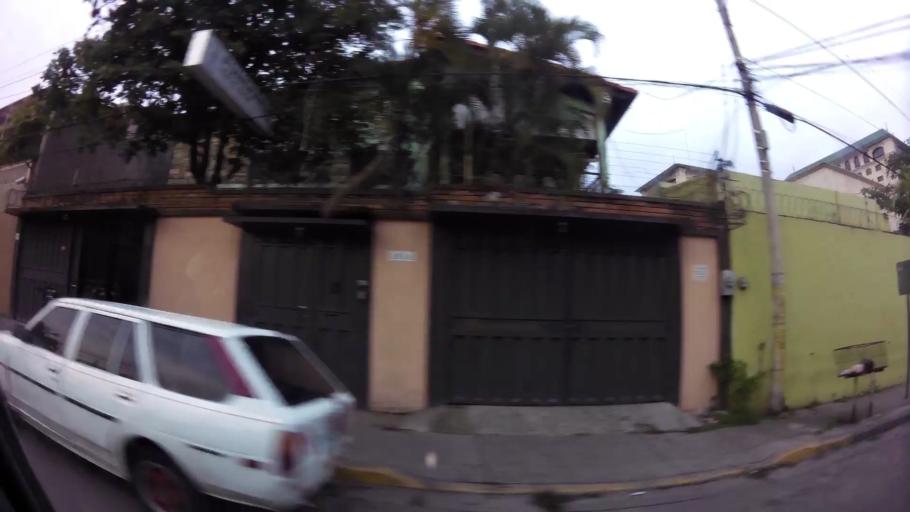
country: HN
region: Francisco Morazan
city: Tegucigalpa
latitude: 14.0913
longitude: -87.1953
